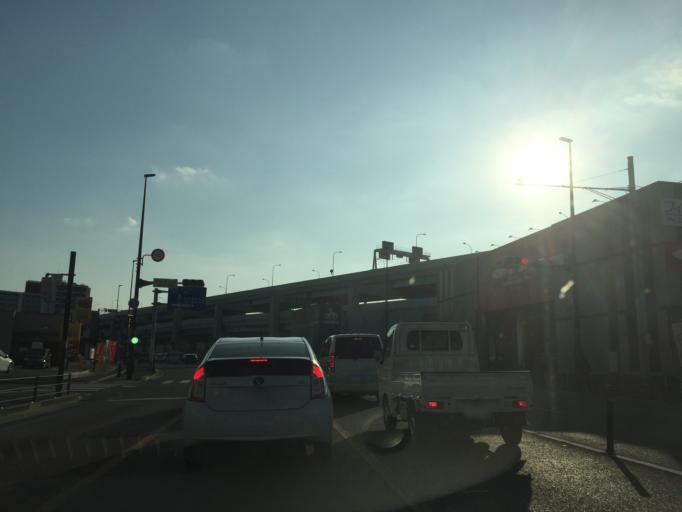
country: JP
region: Fukuoka
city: Fukuoka-shi
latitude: 33.6072
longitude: 130.4098
